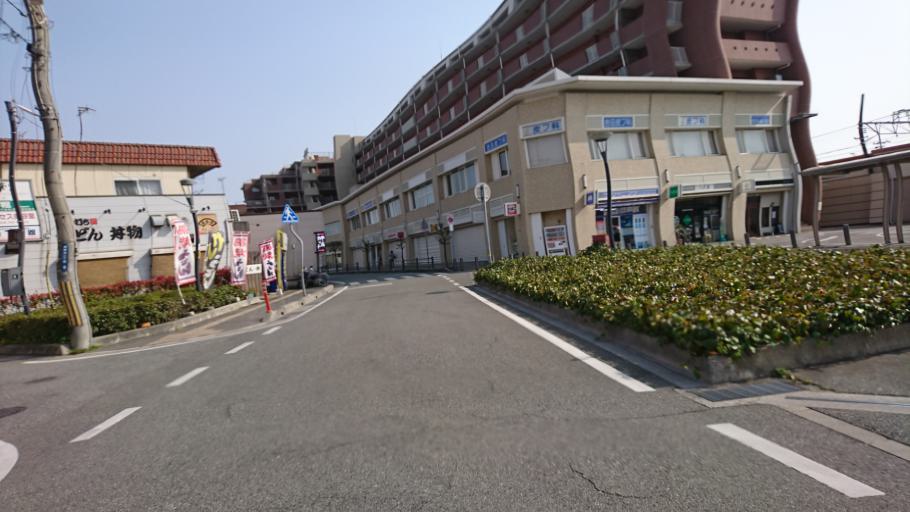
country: JP
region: Hyogo
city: Kakogawacho-honmachi
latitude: 34.7170
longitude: 134.8685
